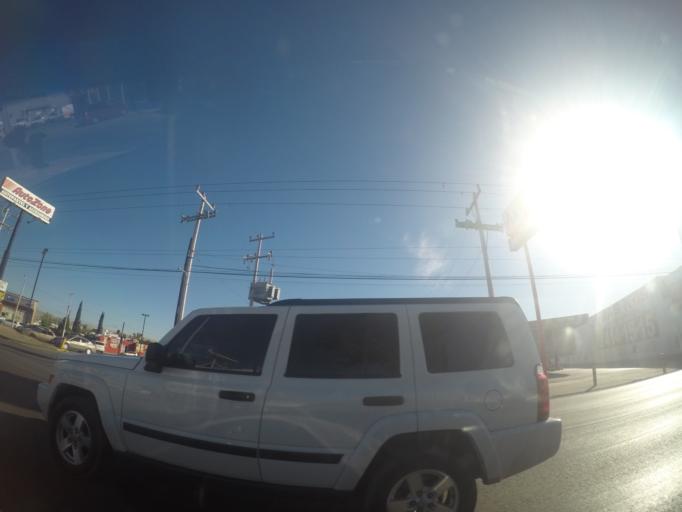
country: MX
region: Chihuahua
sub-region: Chihuahua
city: Chihuahua
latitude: 28.6713
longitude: -106.0965
